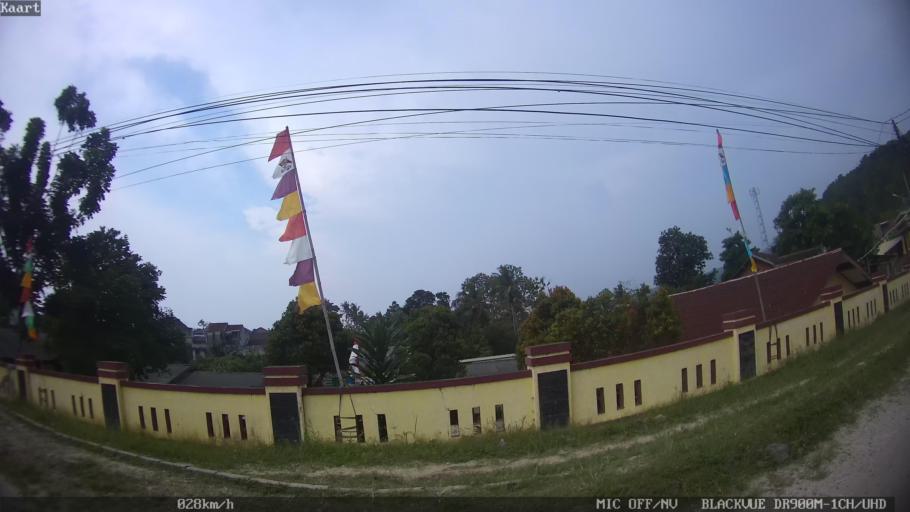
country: ID
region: Lampung
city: Bandarlampung
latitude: -5.4224
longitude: 105.2826
